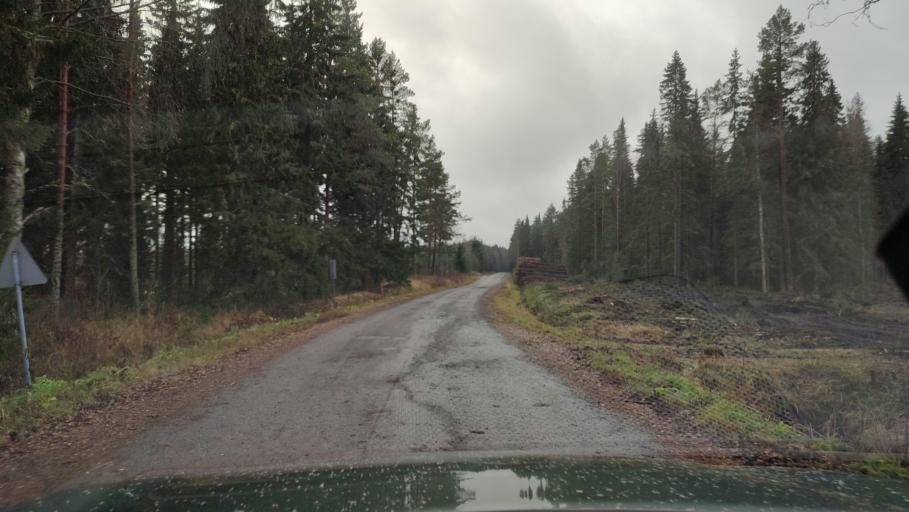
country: FI
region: Ostrobothnia
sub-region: Sydosterbotten
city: Naerpes
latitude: 62.4579
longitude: 21.4868
